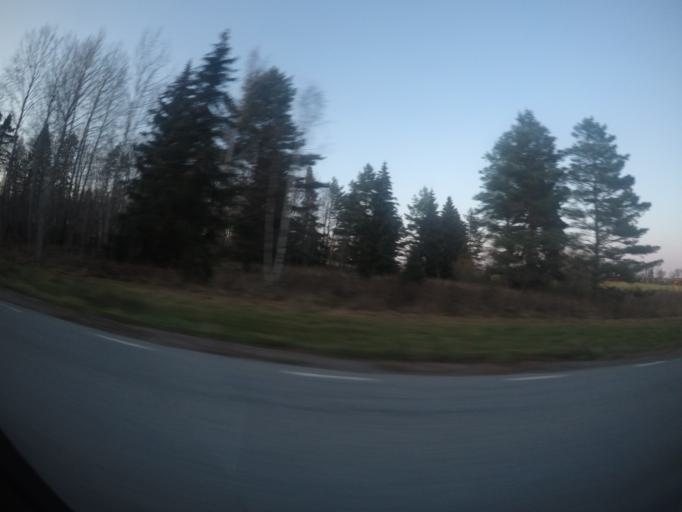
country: SE
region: OErebro
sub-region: Orebro Kommun
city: Hovsta
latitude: 59.3145
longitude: 15.3135
